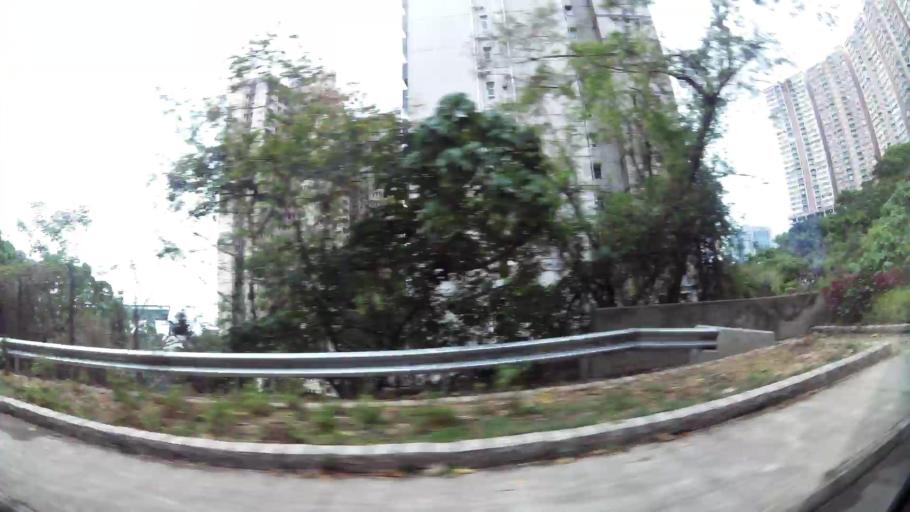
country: HK
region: Central and Western
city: Central
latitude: 22.2611
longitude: 114.1338
